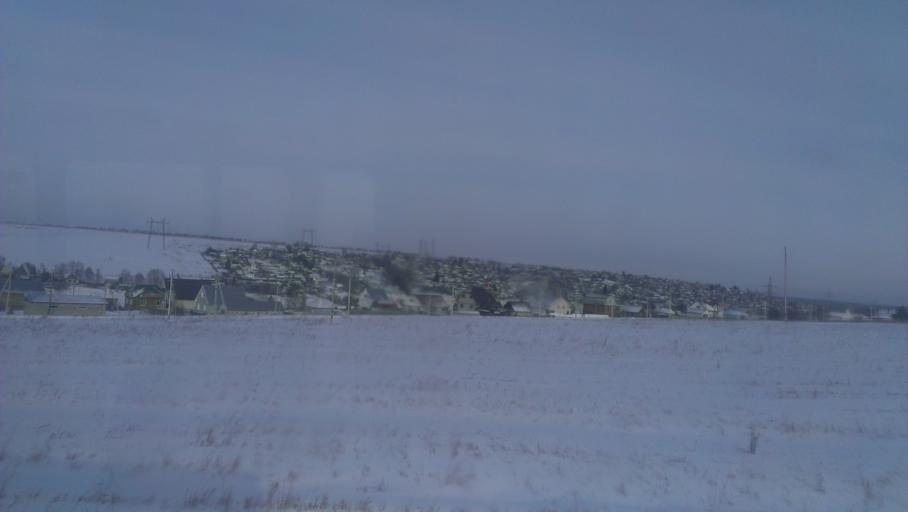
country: RU
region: Altai Krai
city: Gon'ba
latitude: 53.4129
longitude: 83.5558
